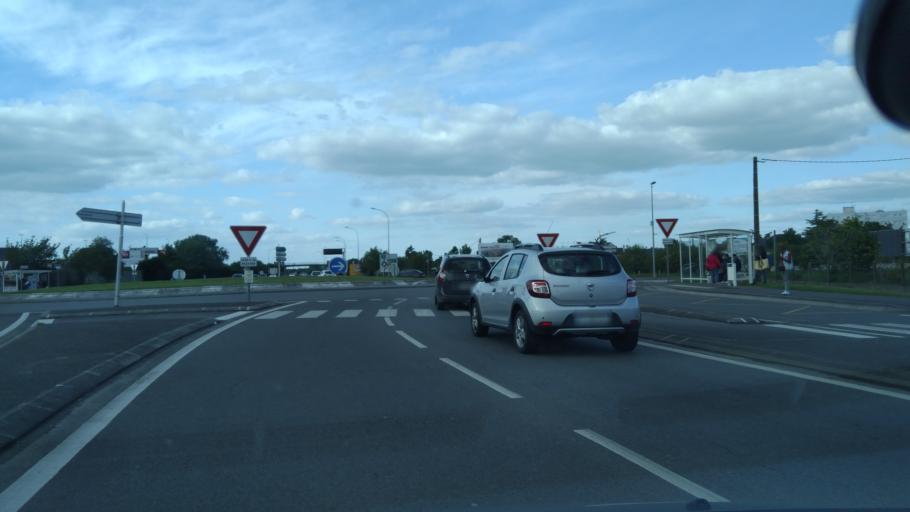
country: FR
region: Pays de la Loire
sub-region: Departement de la Loire-Atlantique
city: Saint-Nazaire
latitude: 47.2986
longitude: -2.2074
